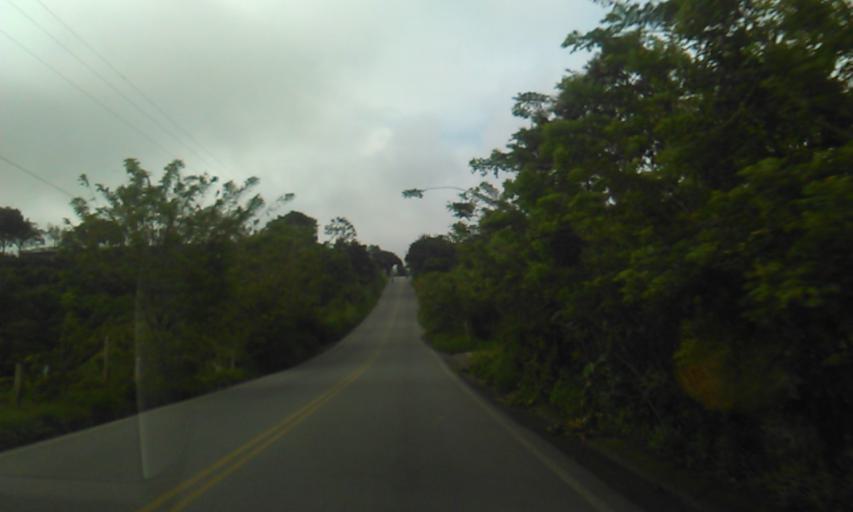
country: CO
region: Quindio
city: Cordoba
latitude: 4.4223
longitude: -75.7219
